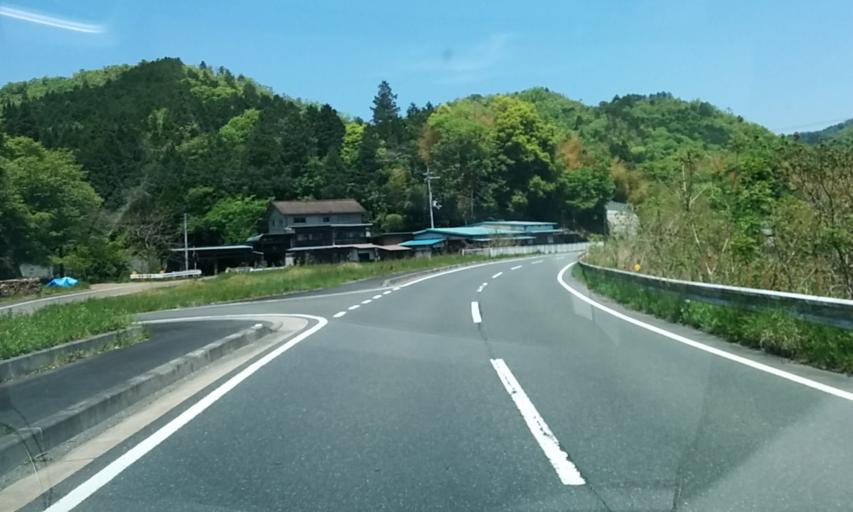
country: JP
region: Kyoto
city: Ayabe
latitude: 35.2483
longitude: 135.2670
